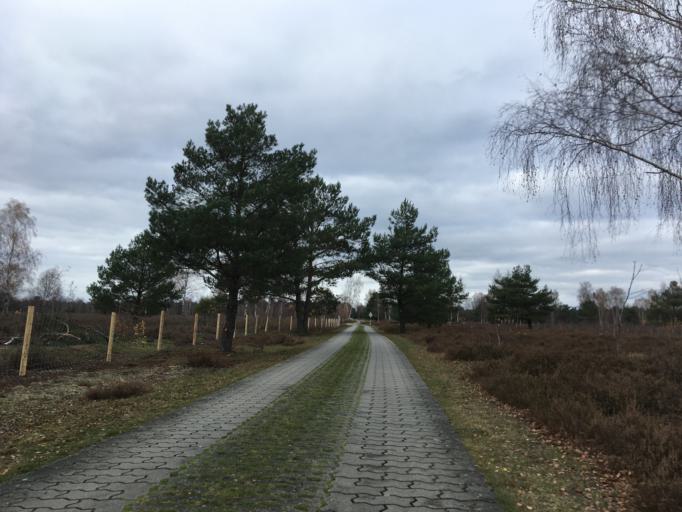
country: DE
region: Brandenburg
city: Tauer
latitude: 52.0102
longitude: 14.4940
